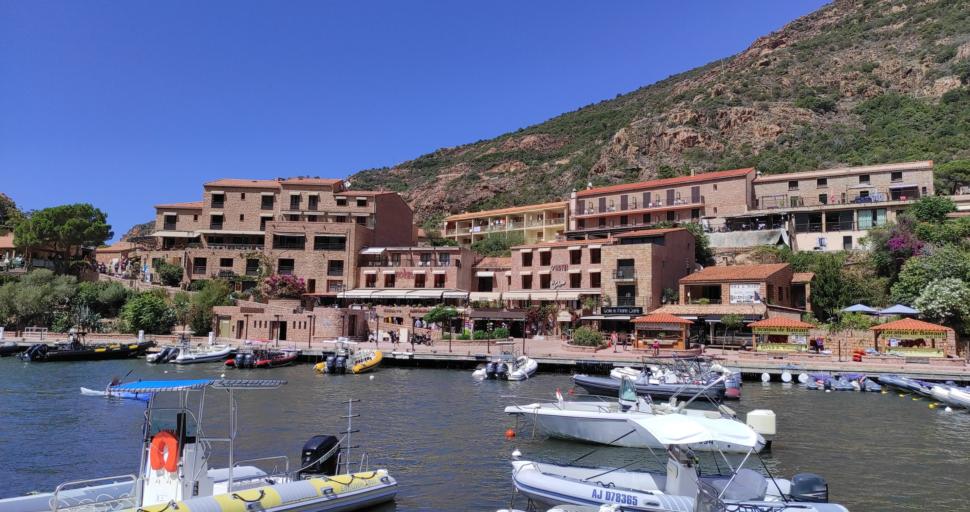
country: FR
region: Corsica
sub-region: Departement de la Corse-du-Sud
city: Cargese
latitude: 42.2665
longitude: 8.6939
